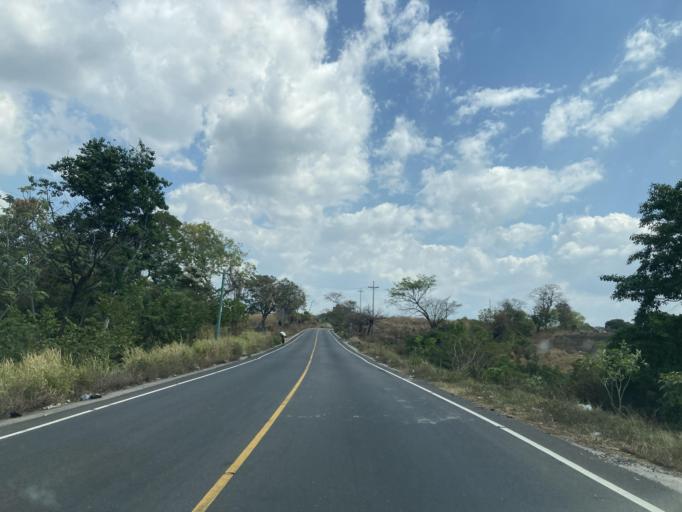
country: GT
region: Santa Rosa
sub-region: Municipio de Taxisco
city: Taxisco
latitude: 14.0625
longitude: -90.4656
